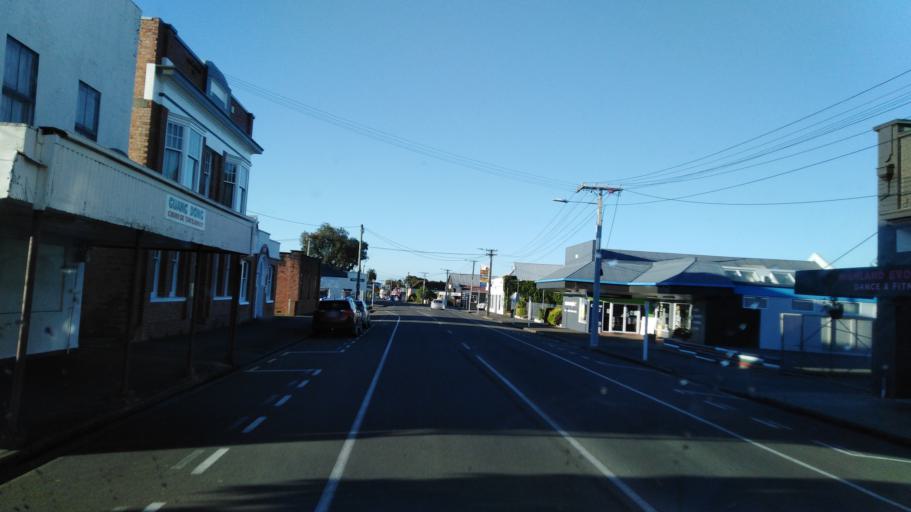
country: NZ
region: Manawatu-Wanganui
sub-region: Rangitikei District
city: Bulls
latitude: -40.0693
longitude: 175.3784
